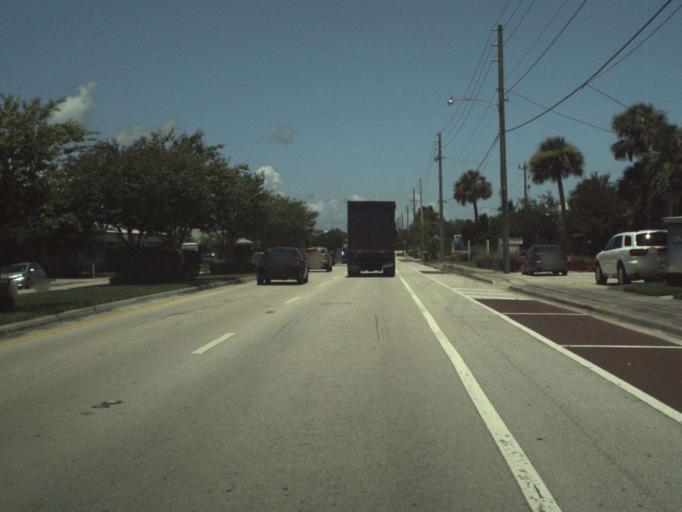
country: US
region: Florida
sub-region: Indian River County
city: Sebastian
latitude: 27.8210
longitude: -80.4718
